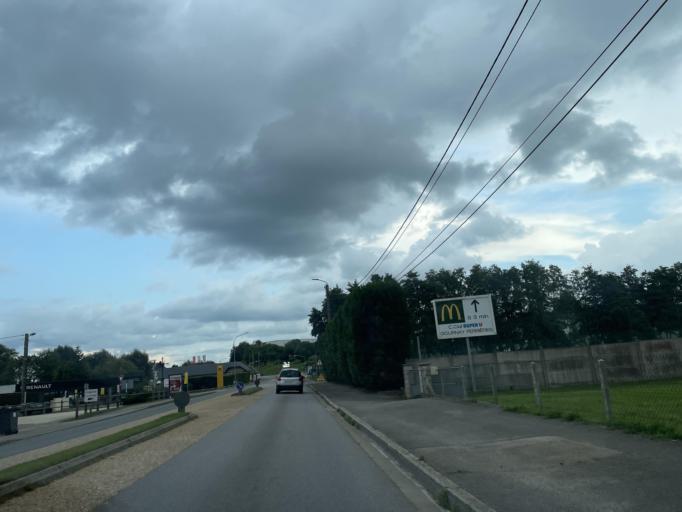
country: FR
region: Haute-Normandie
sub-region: Departement de la Seine-Maritime
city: Gournay-en-Bray
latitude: 49.4839
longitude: 1.7105
